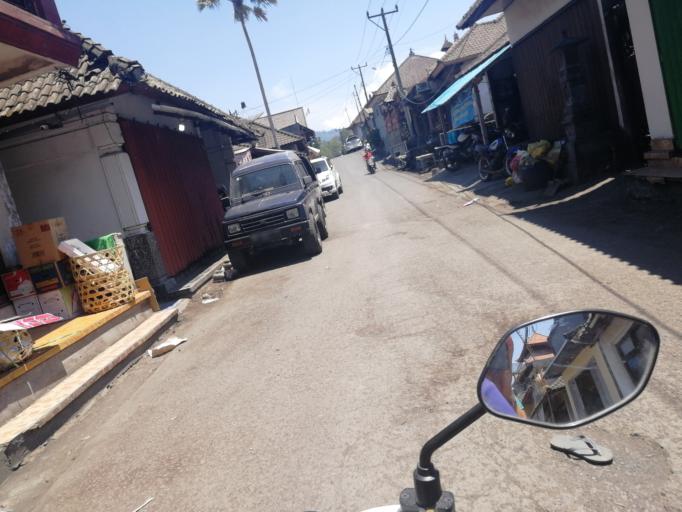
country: ID
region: Bali
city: Banjar Trunyan
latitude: -8.2269
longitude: 115.4095
